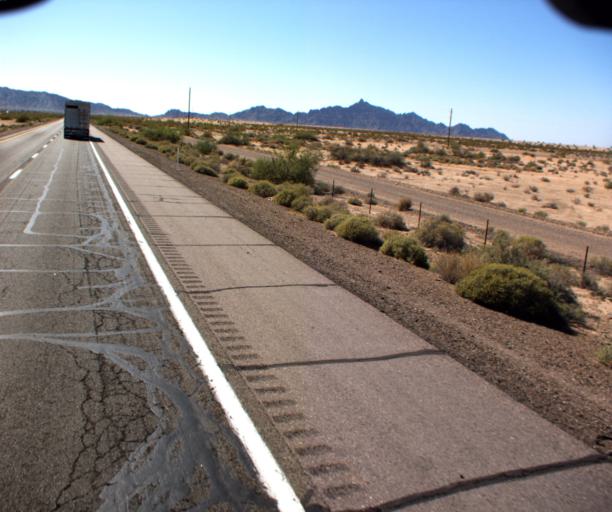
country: US
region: Arizona
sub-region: Yuma County
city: Wellton
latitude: 32.7495
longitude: -113.6656
